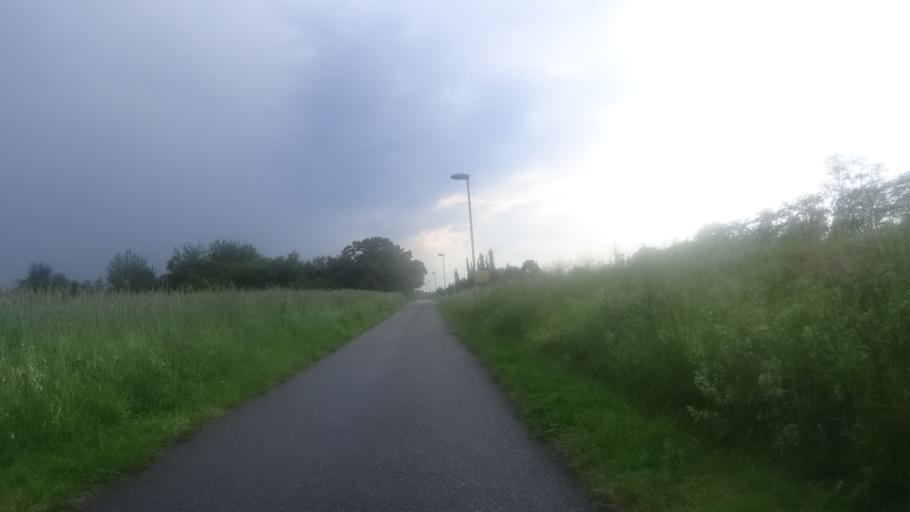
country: DE
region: Baden-Wuerttemberg
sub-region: Karlsruhe Region
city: Bietigheim
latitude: 48.9178
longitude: 8.2583
